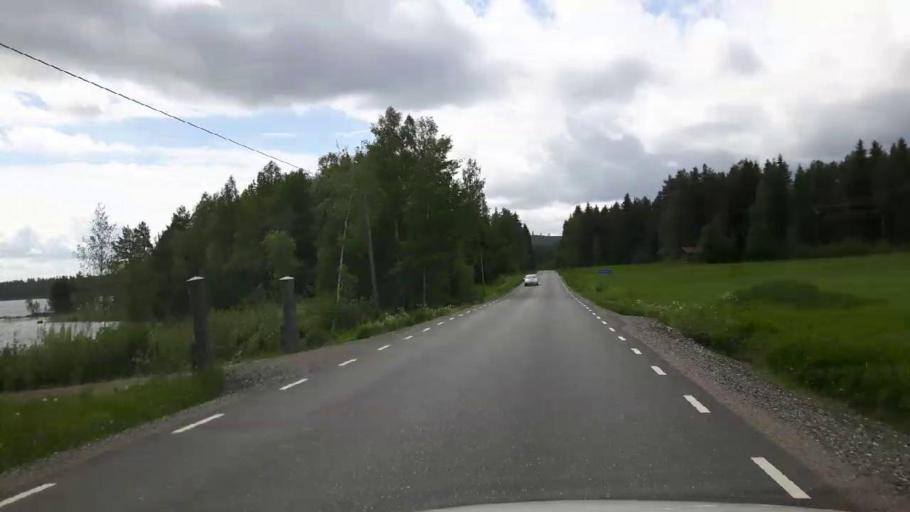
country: SE
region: Dalarna
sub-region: Faluns Kommun
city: Falun
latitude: 60.6814
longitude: 15.7647
